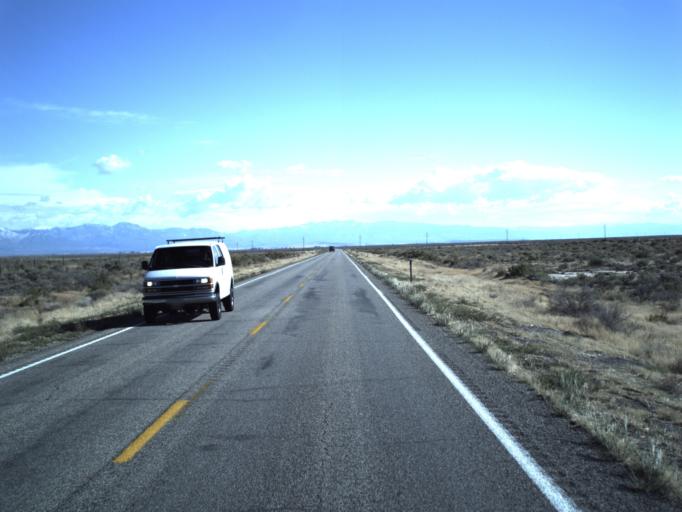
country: US
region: Utah
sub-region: Millard County
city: Delta
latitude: 39.3049
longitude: -112.4739
